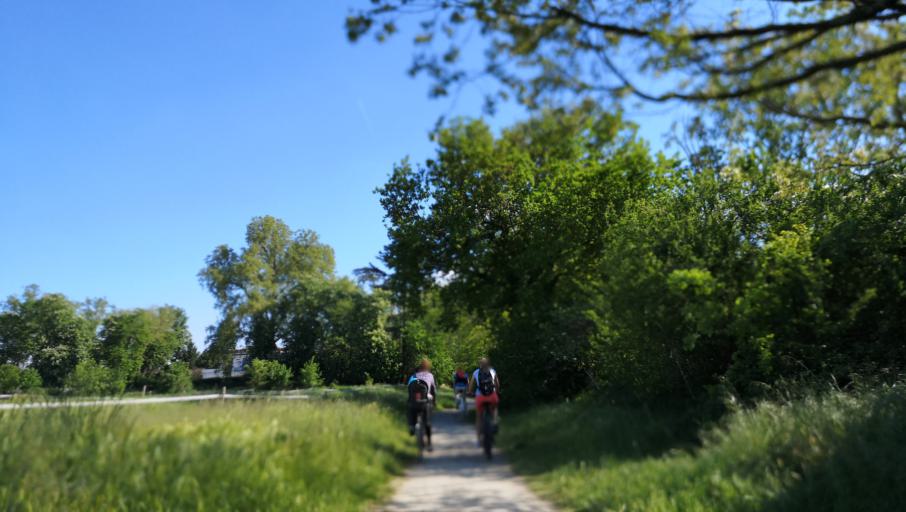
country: FR
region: Midi-Pyrenees
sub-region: Departement de la Haute-Garonne
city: Blagnac
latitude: 43.6413
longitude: 1.4040
